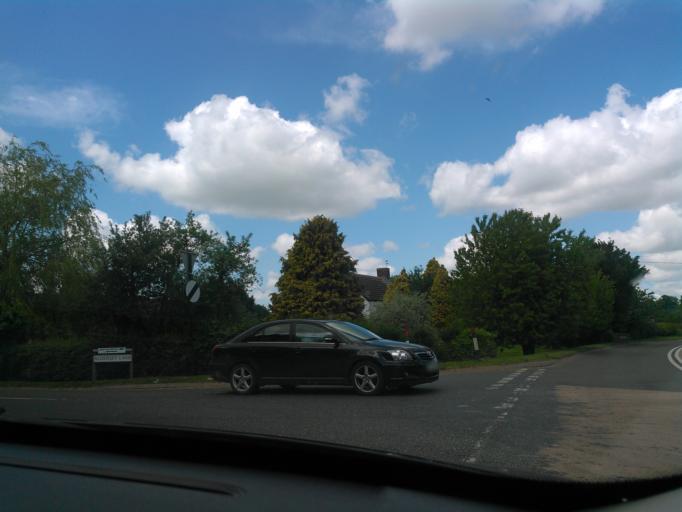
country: GB
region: England
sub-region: Shropshire
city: Prees
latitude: 52.8848
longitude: -2.6611
